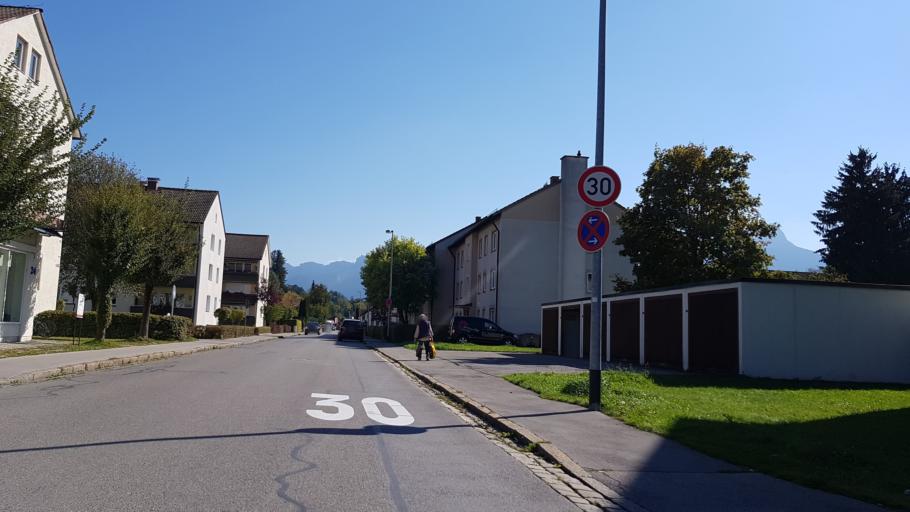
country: DE
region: Bavaria
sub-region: Swabia
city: Fuessen
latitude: 47.5734
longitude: 10.6781
